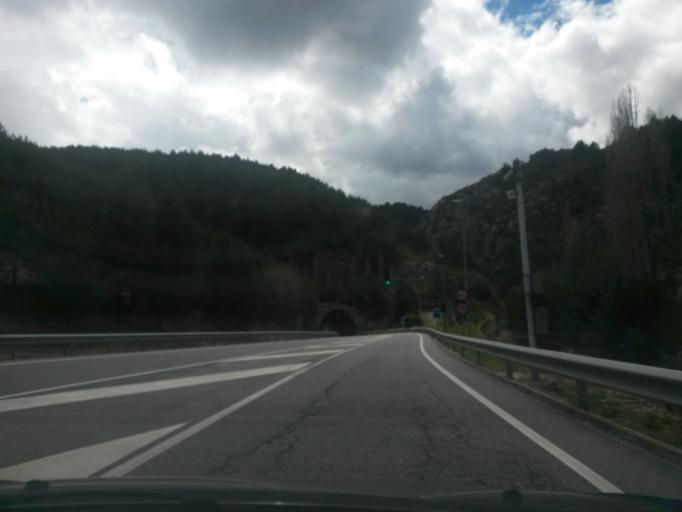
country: ES
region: Catalonia
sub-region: Provincia de Lleida
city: Riu de Cerdanya
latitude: 42.3365
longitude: 1.8386
